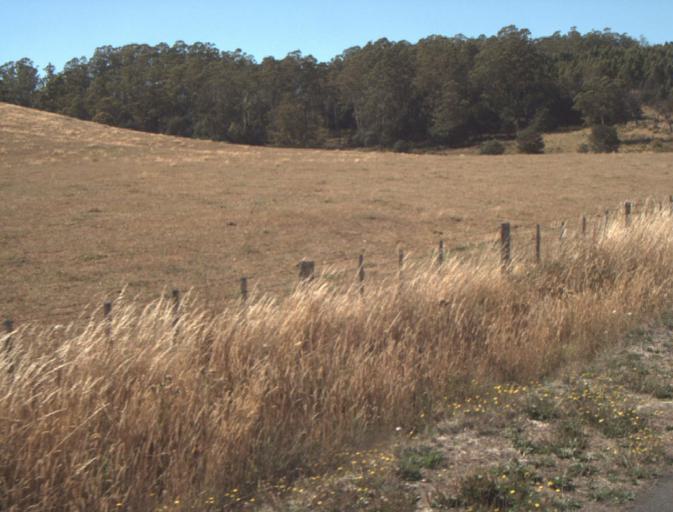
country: AU
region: Tasmania
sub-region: Launceston
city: Newstead
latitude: -41.3468
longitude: 147.3030
